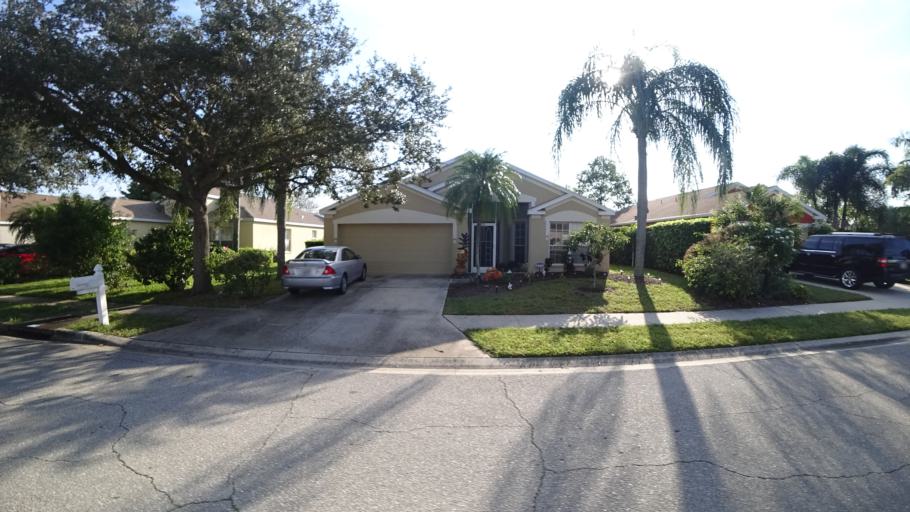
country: US
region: Florida
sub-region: Manatee County
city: Samoset
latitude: 27.4571
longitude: -82.5021
